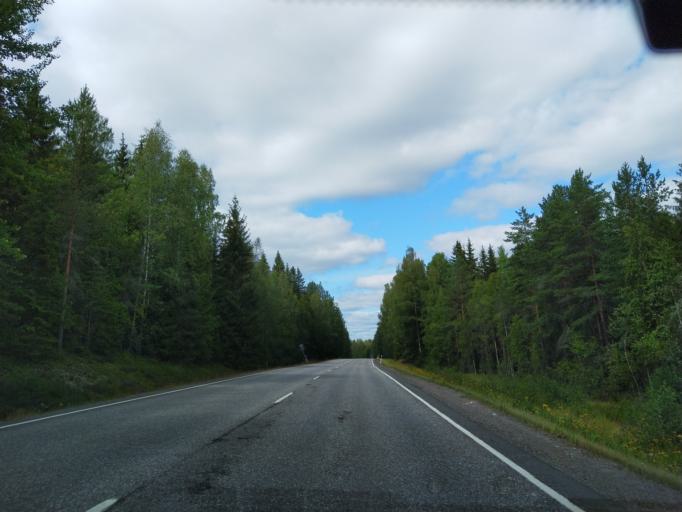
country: FI
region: Haeme
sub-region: Riihimaeki
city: Loppi
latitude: 60.7276
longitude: 24.4045
